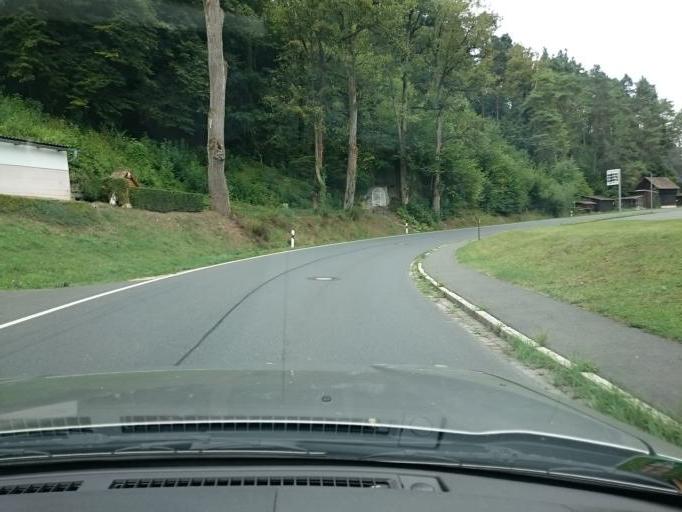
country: DE
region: Bavaria
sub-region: Regierungsbezirk Mittelfranken
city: Neuhaus an der Pegnitz
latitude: 49.6314
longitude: 11.5458
